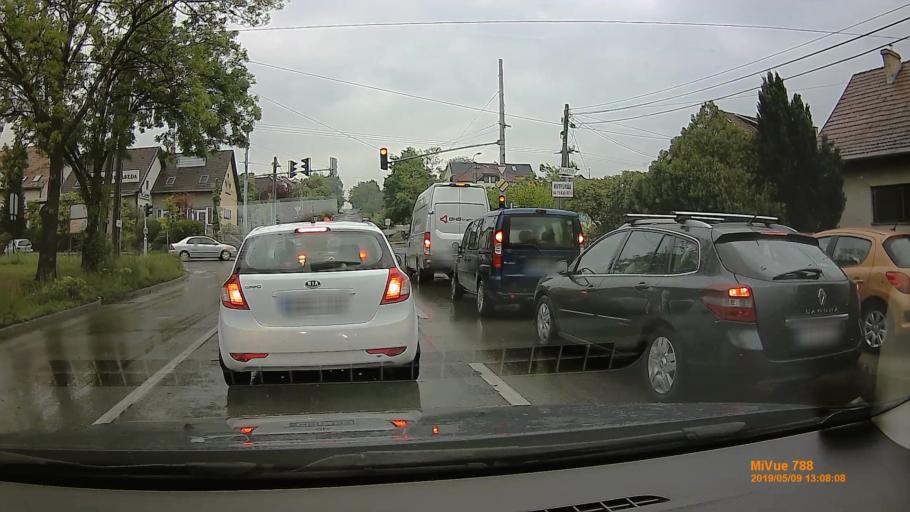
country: HU
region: Budapest
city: Budapest XVI. keruelet
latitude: 47.5348
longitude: 19.1810
